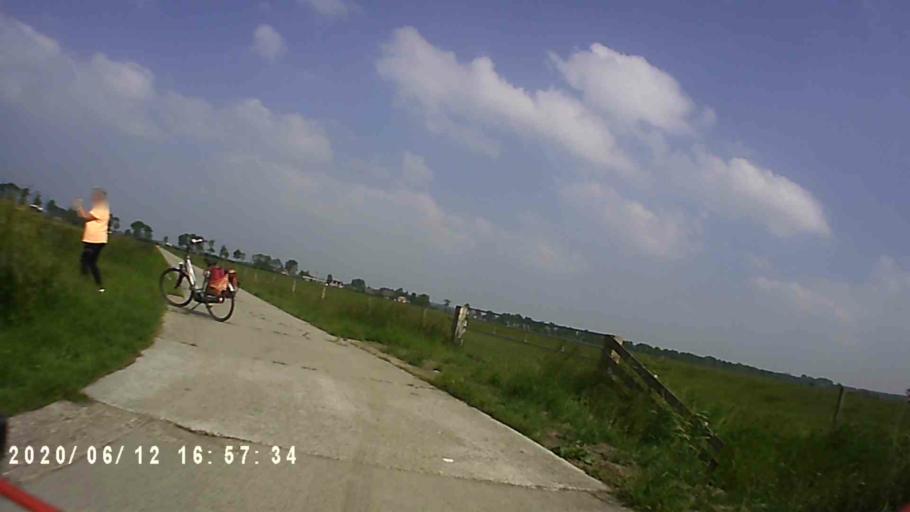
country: NL
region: Groningen
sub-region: Gemeente Groningen
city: Korrewegwijk
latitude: 53.2647
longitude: 6.5585
